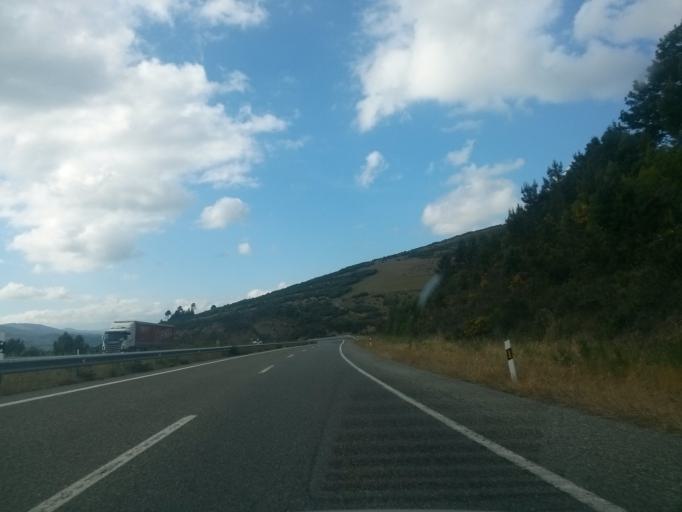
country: ES
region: Galicia
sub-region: Provincia de Lugo
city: Becerrea
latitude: 42.9046
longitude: -7.1908
